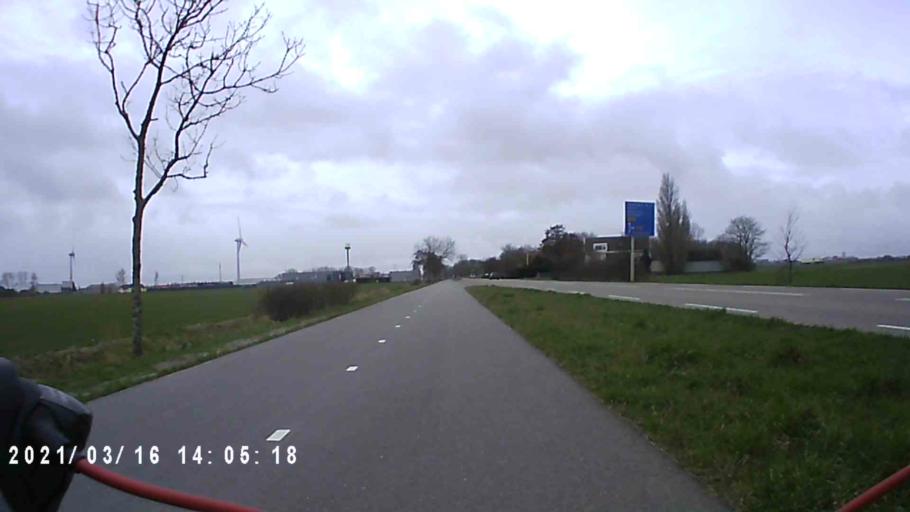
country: NL
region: Friesland
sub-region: Gemeente Franekeradeel
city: Sexbierum
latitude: 53.1831
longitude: 5.4681
